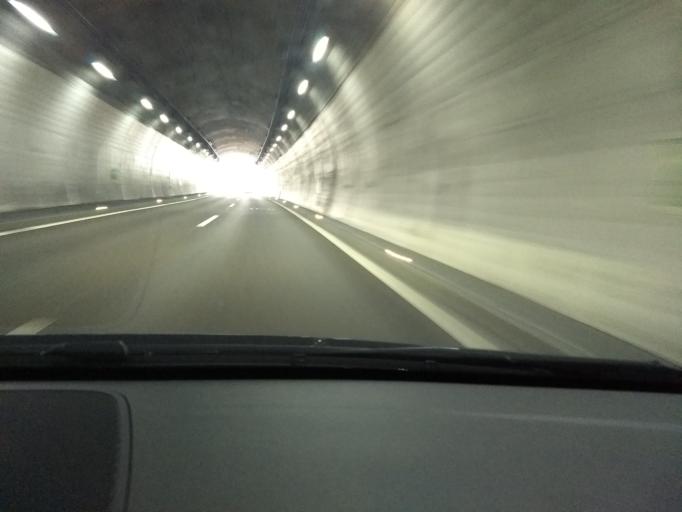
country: CH
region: Basel-Landschaft
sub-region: Bezirk Waldenburg
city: Diegten
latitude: 47.3958
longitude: 7.8146
